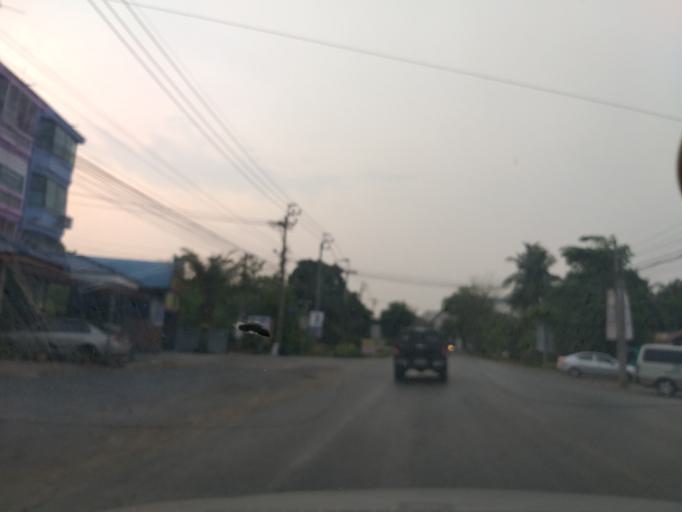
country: TH
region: Bangkok
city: Nong Chok
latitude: 13.8475
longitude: 100.8923
